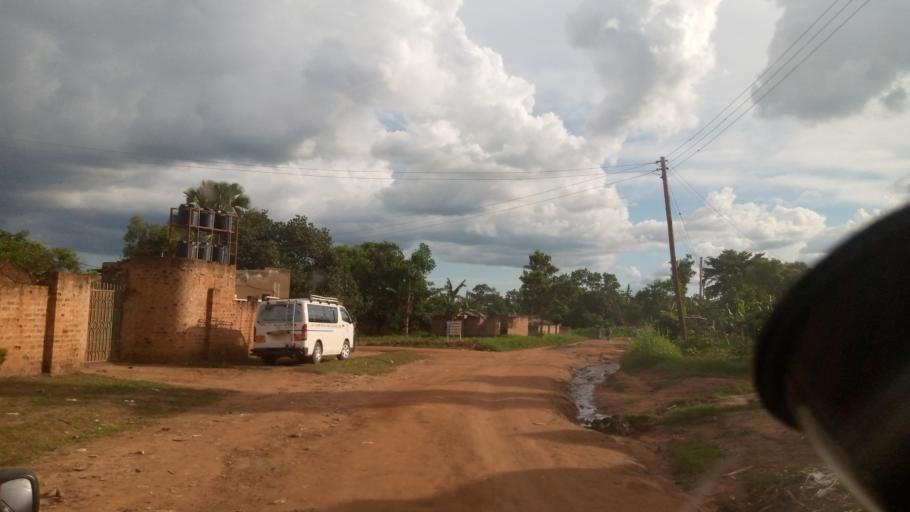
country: UG
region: Northern Region
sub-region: Lira District
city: Lira
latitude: 2.2274
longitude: 32.8925
